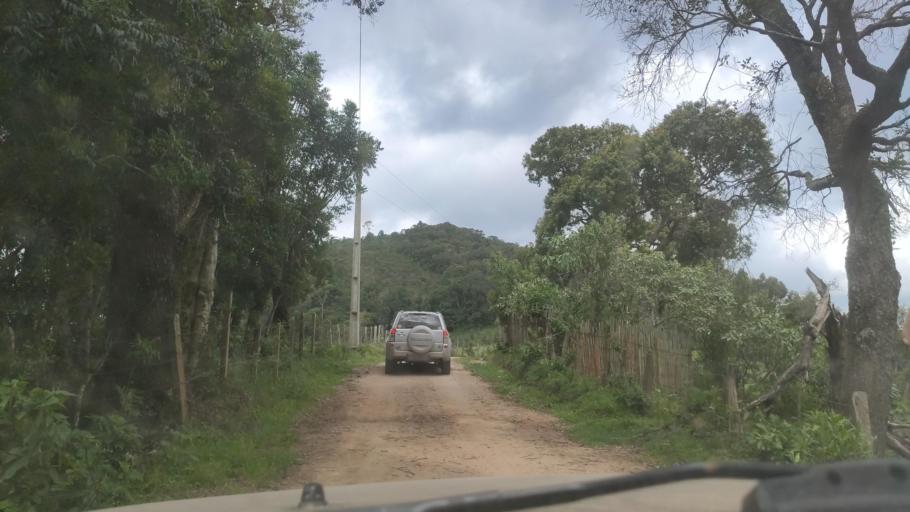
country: BR
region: Minas Gerais
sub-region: Cambui
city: Cambui
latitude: -22.6865
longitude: -45.9575
